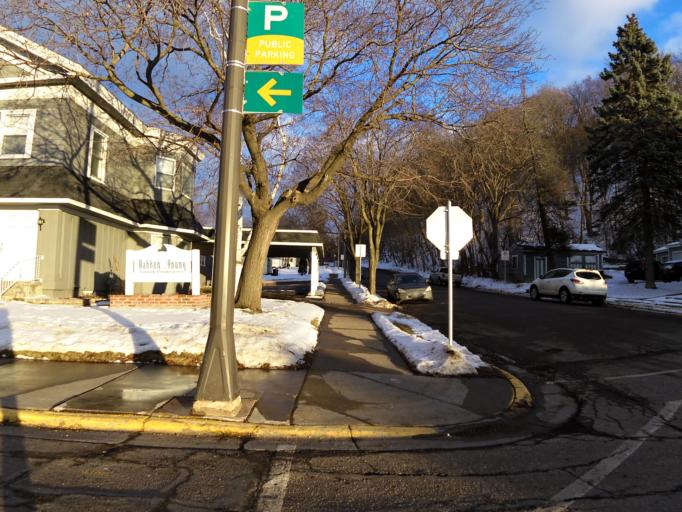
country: US
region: Wisconsin
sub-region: Saint Croix County
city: Hudson
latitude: 44.9750
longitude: -92.7554
